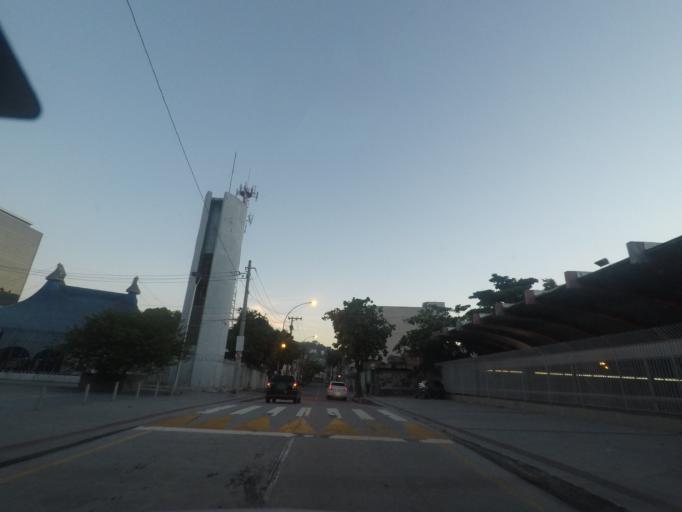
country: BR
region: Rio de Janeiro
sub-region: Rio De Janeiro
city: Rio de Janeiro
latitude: -22.9097
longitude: -43.2001
